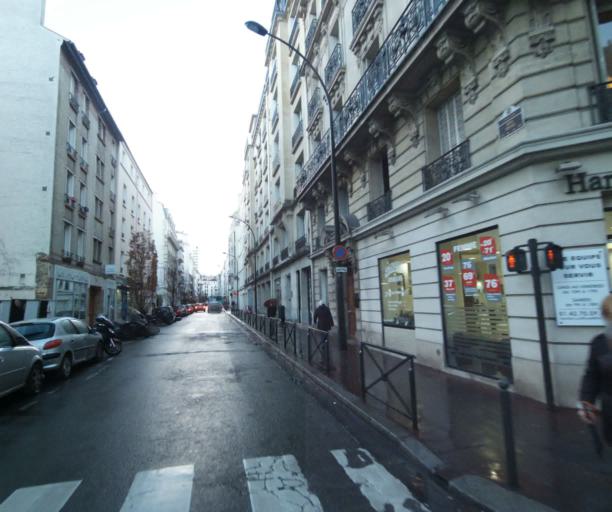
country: FR
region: Ile-de-France
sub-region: Departement des Hauts-de-Seine
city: Levallois-Perret
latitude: 48.8933
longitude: 2.2904
